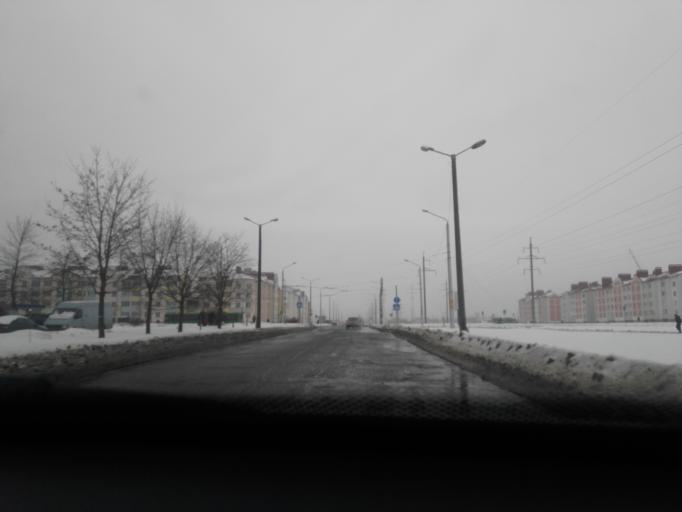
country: BY
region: Mogilev
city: Babruysk
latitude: 53.1978
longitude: 29.2214
